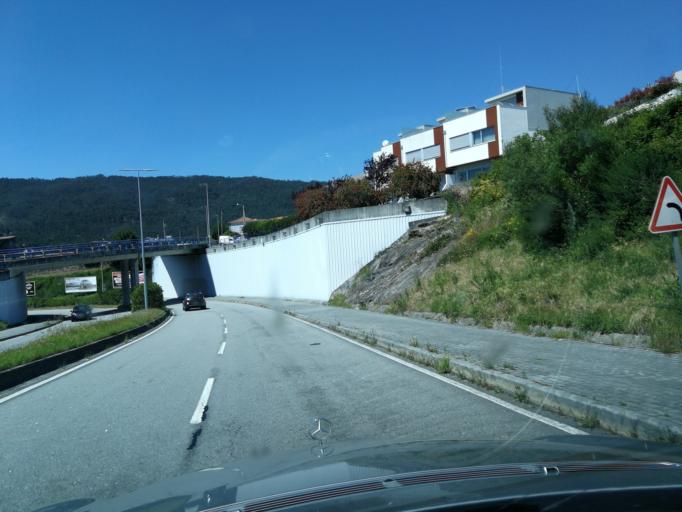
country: PT
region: Viana do Castelo
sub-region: Viana do Castelo
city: Meadela
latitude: 41.7108
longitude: -8.8088
